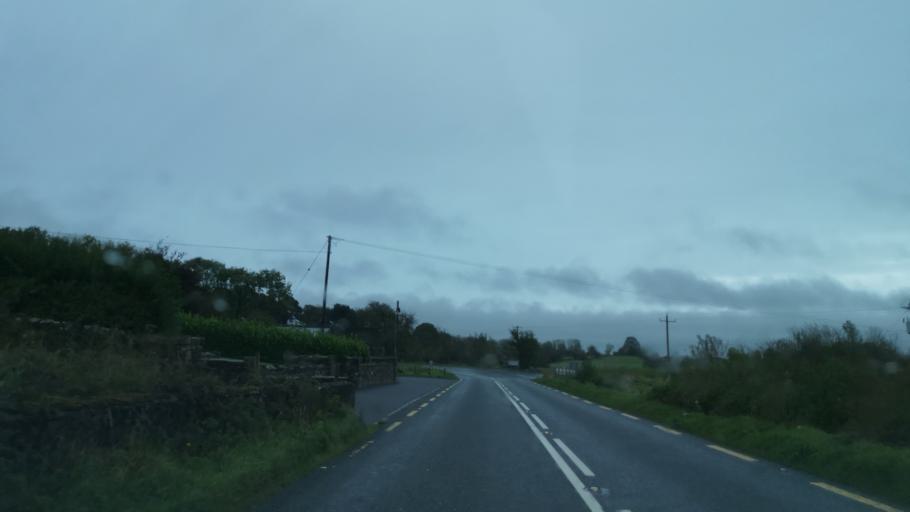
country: IE
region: Connaught
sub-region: Maigh Eo
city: Ballyhaunis
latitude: 53.7700
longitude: -8.7625
